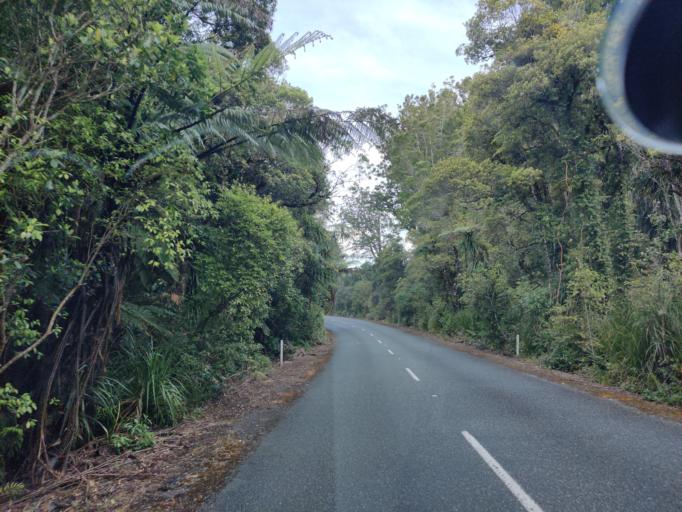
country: NZ
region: Northland
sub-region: Far North District
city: Waimate North
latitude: -35.6047
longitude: 173.5329
